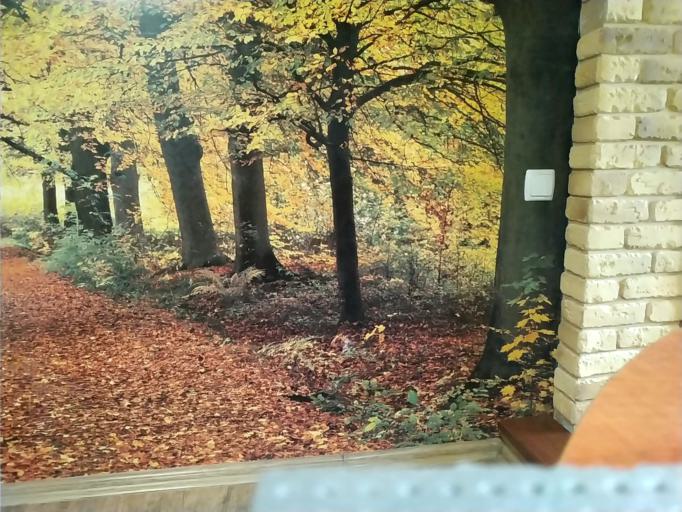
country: RU
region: Tverskaya
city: Staritsa
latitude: 56.5405
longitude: 34.9701
